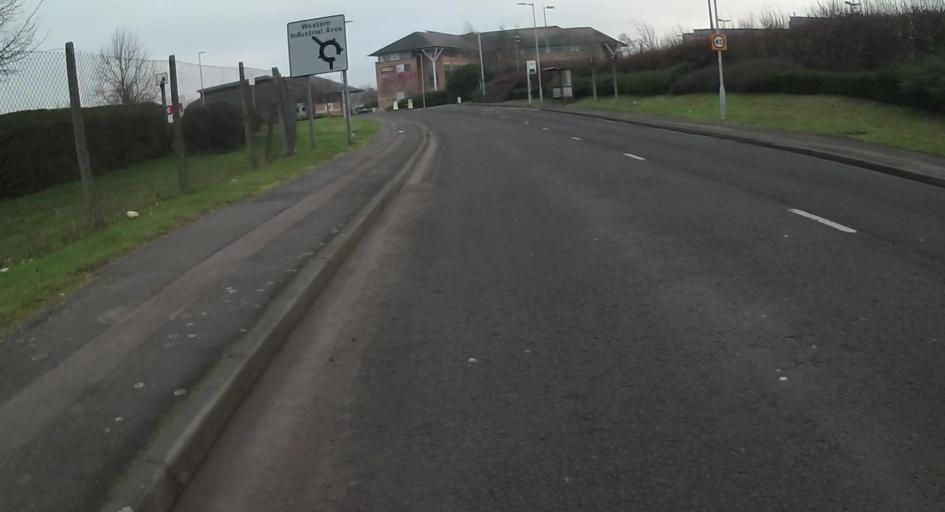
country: GB
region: England
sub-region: Bracknell Forest
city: Binfield
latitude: 51.4148
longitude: -0.7805
